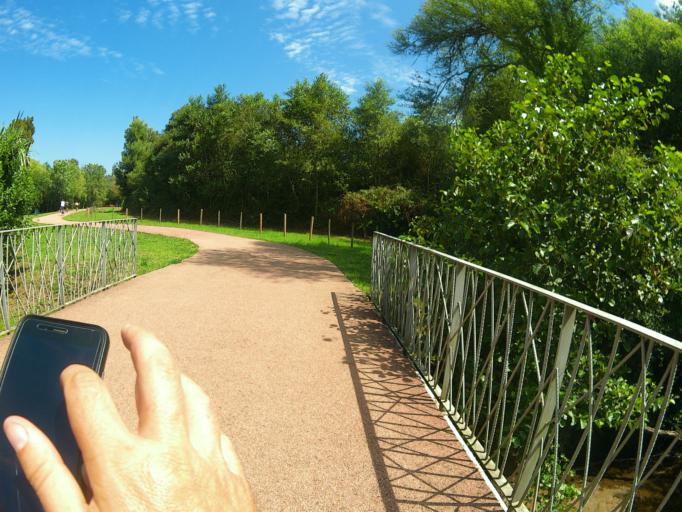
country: PT
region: Viana do Castelo
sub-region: Vila Nova de Cerveira
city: Vila Nova de Cerveira
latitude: 41.9341
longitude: -8.7522
